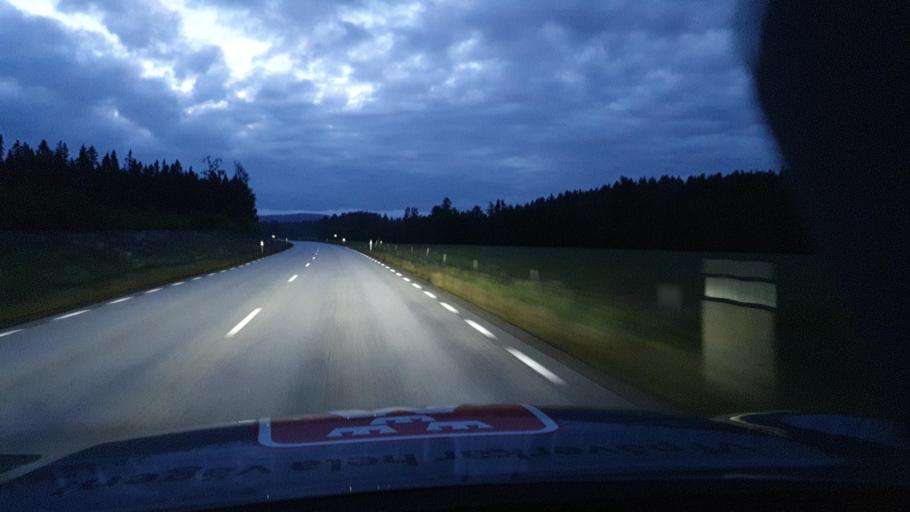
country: SE
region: Vaermland
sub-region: Storfors Kommun
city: Storfors
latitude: 59.4843
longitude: 14.3288
